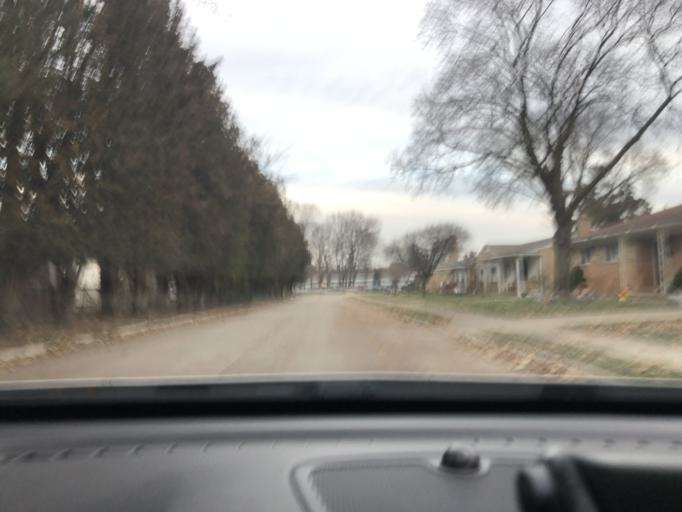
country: US
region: Michigan
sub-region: Wayne County
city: Allen Park
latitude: 42.2854
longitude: -83.2245
